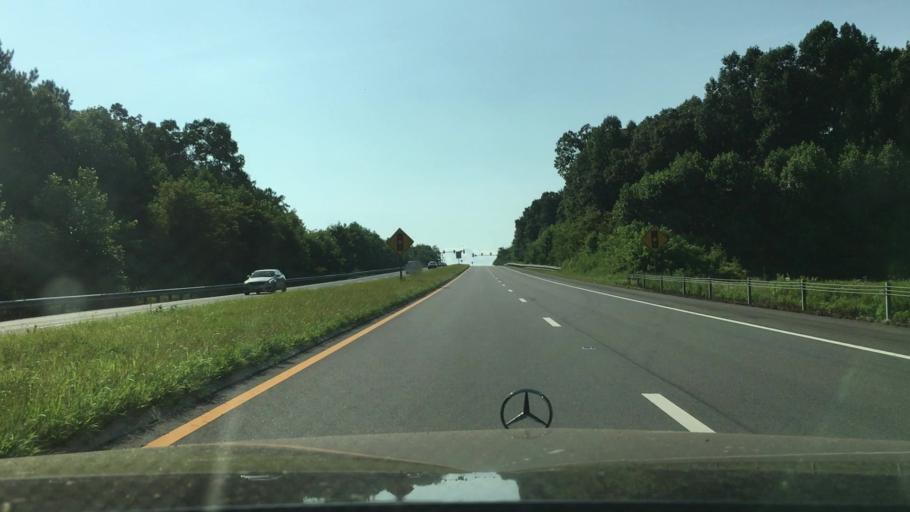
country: US
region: Virginia
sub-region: Amherst County
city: Madison Heights
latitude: 37.4187
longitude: -79.1162
